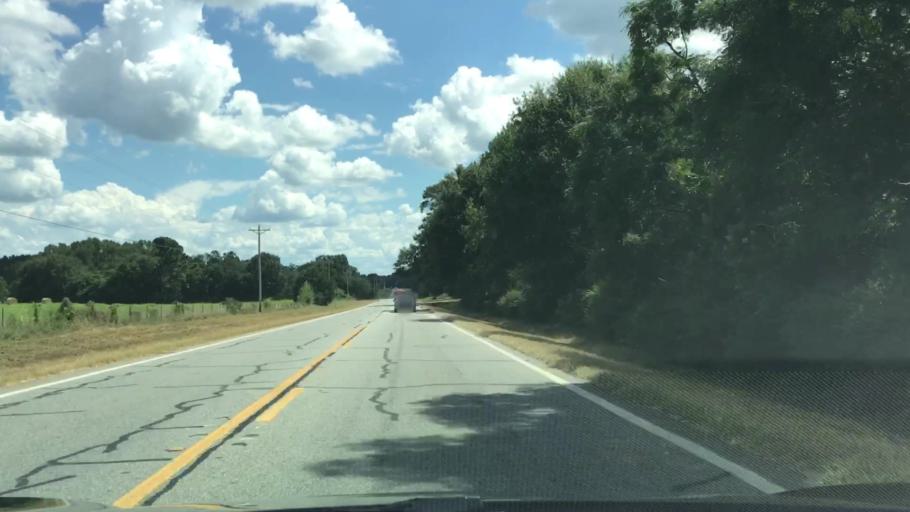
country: US
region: Georgia
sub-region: Oconee County
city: Watkinsville
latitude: 33.8233
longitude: -83.3696
